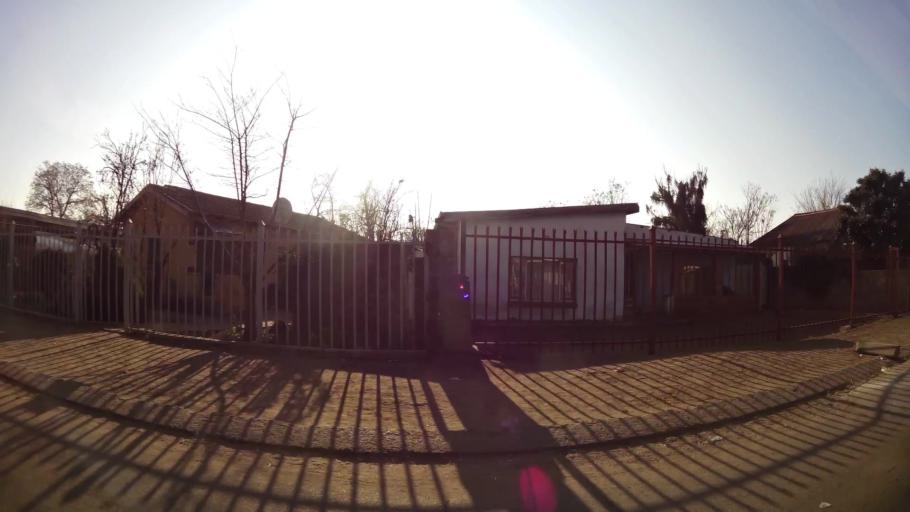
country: ZA
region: Orange Free State
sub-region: Mangaung Metropolitan Municipality
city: Bloemfontein
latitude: -29.1335
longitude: 26.2399
